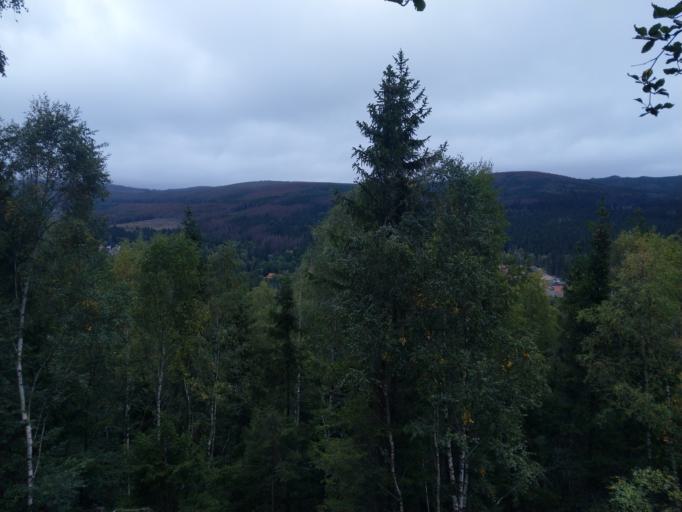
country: DE
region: Lower Saxony
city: Braunlage
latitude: 51.7541
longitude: 10.6712
